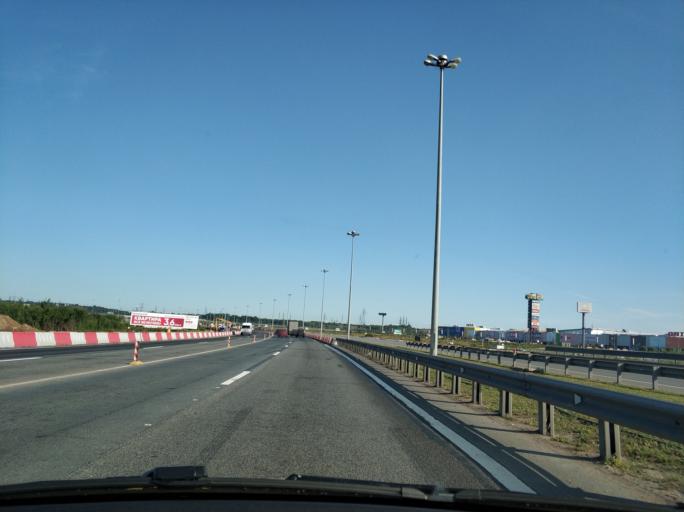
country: RU
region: Leningrad
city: Bugry
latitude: 60.0849
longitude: 30.3777
